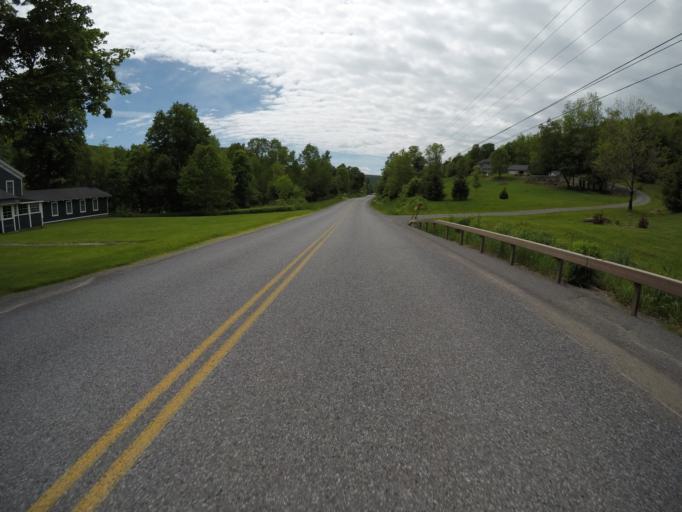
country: US
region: New York
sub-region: Delaware County
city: Stamford
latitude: 42.2030
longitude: -74.5755
